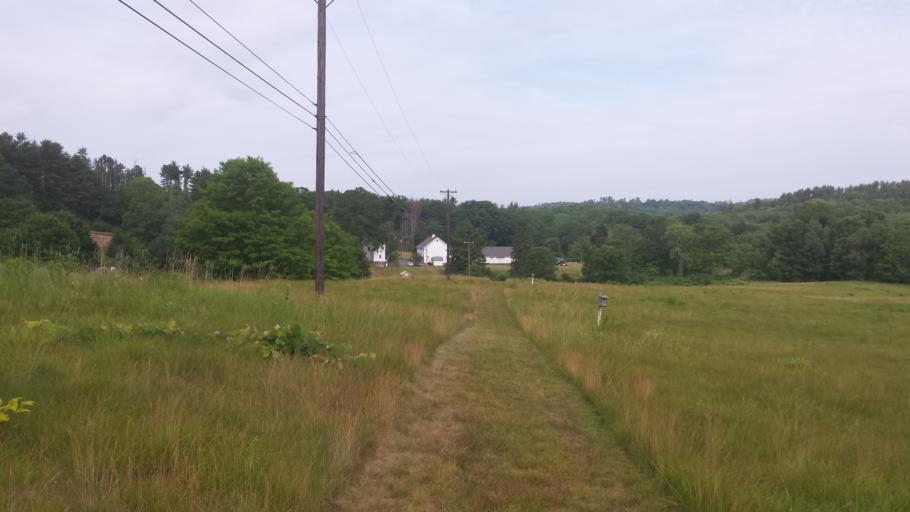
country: US
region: New York
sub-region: Westchester County
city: Pound Ridge
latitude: 41.2581
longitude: -73.5976
